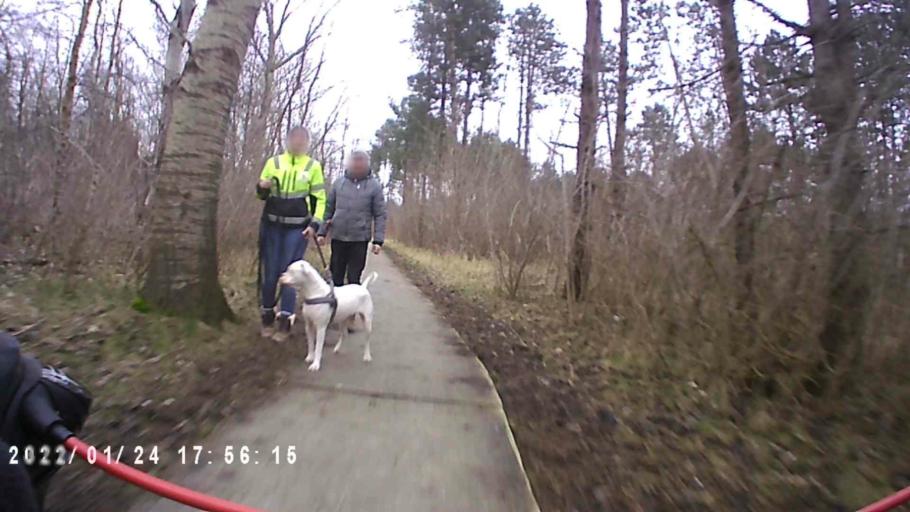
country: NL
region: Groningen
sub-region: Gemeente De Marne
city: Ulrum
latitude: 53.3998
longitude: 6.2352
